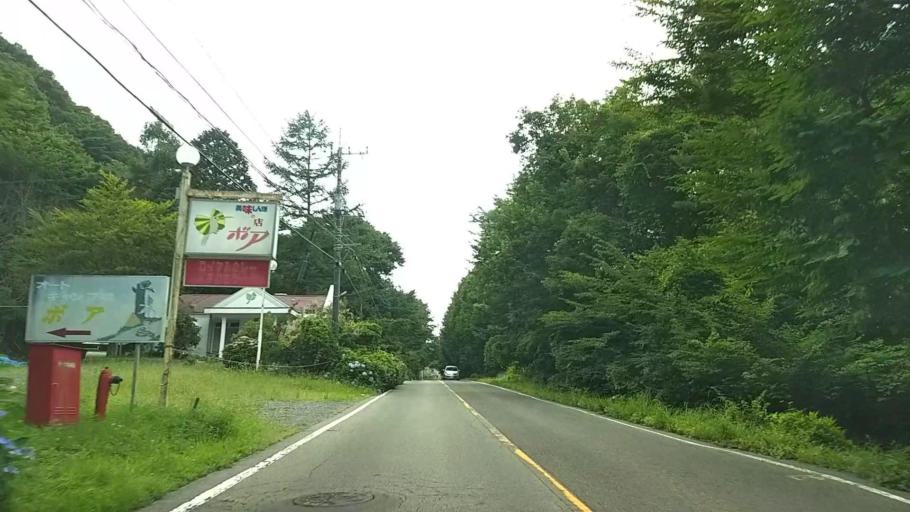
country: JP
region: Yamanashi
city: Fujikawaguchiko
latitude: 35.4923
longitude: 138.6808
